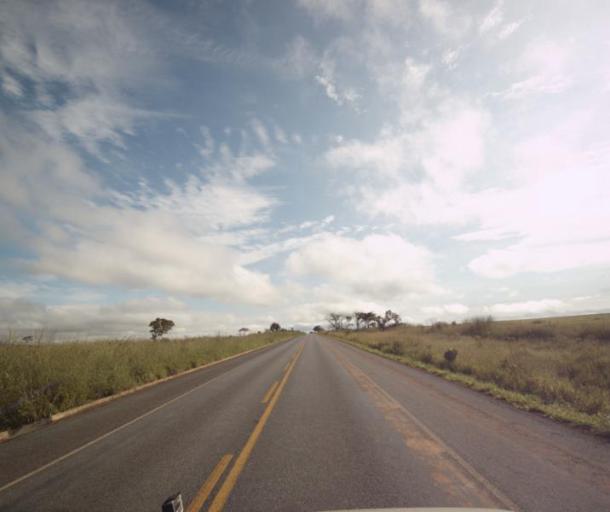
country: BR
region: Goias
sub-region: Padre Bernardo
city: Padre Bernardo
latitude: -15.4684
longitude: -48.6142
